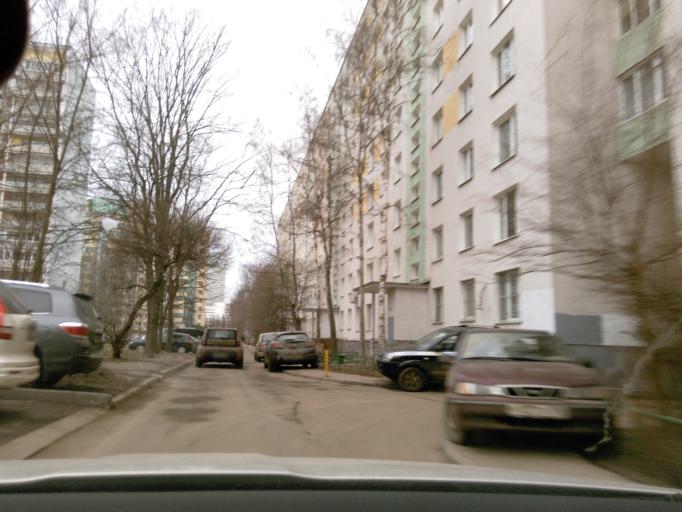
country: RU
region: Moscow
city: Zelenograd
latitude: 55.9973
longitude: 37.2130
